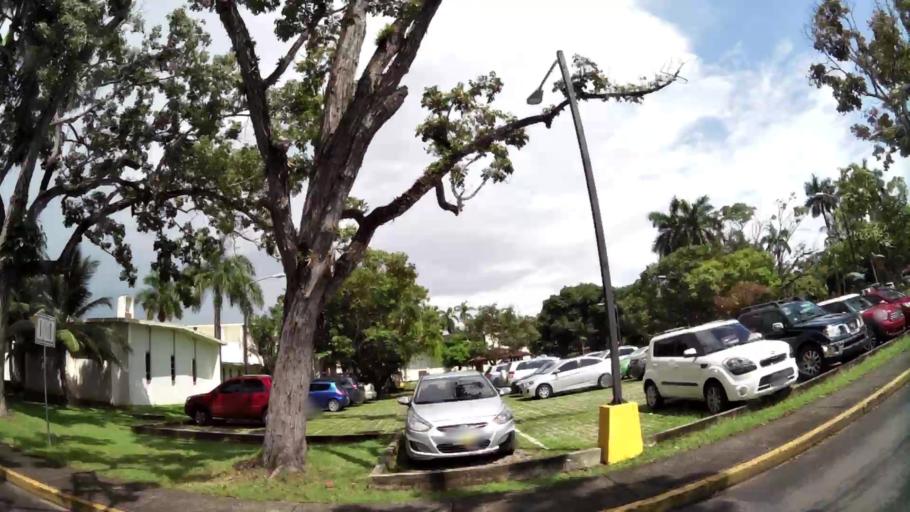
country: PA
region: Panama
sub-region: Distrito de Panama
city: Ancon
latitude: 8.9976
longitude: -79.5835
